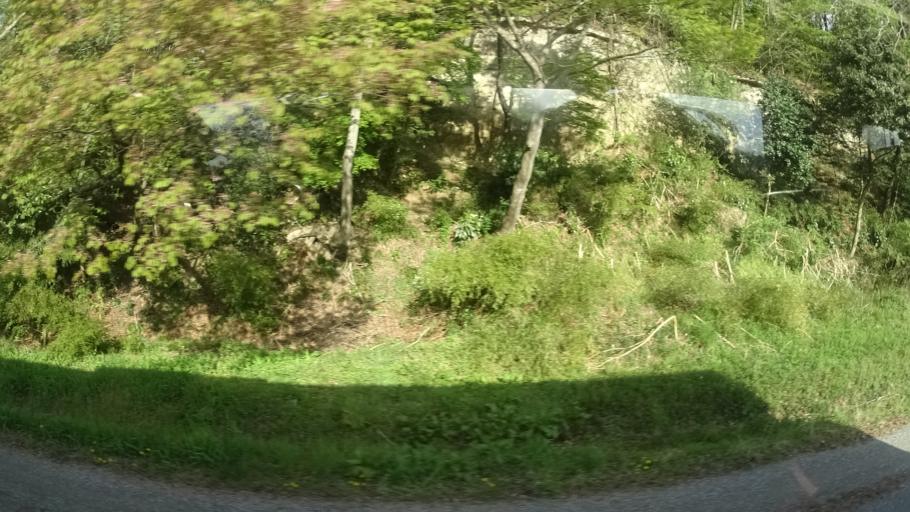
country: JP
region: Fukushima
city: Namie
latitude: 37.5532
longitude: 140.9948
